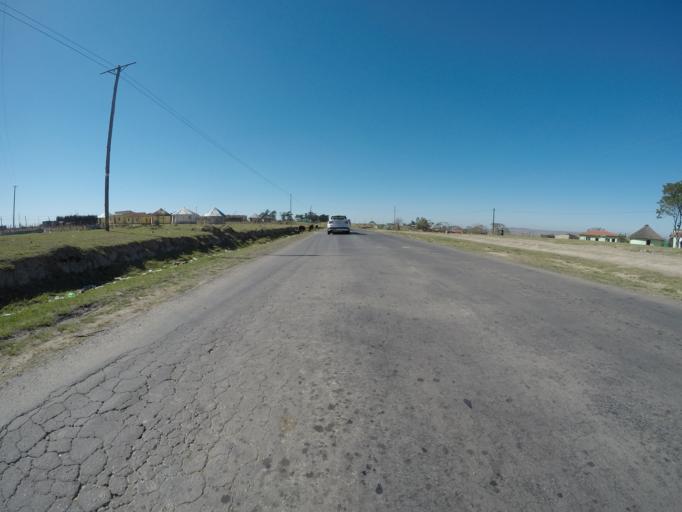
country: ZA
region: Eastern Cape
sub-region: OR Tambo District Municipality
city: Mthatha
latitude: -31.7869
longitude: 28.7426
